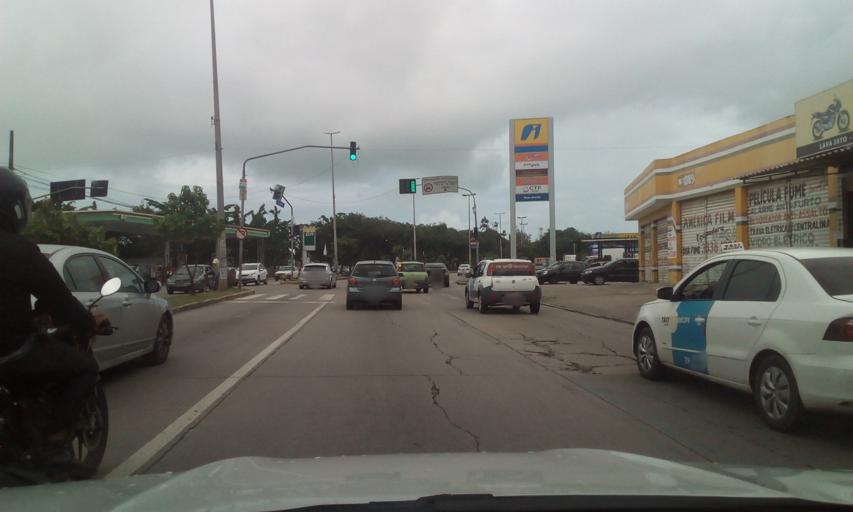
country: BR
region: Pernambuco
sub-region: Recife
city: Recife
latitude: -8.1201
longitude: -34.9199
